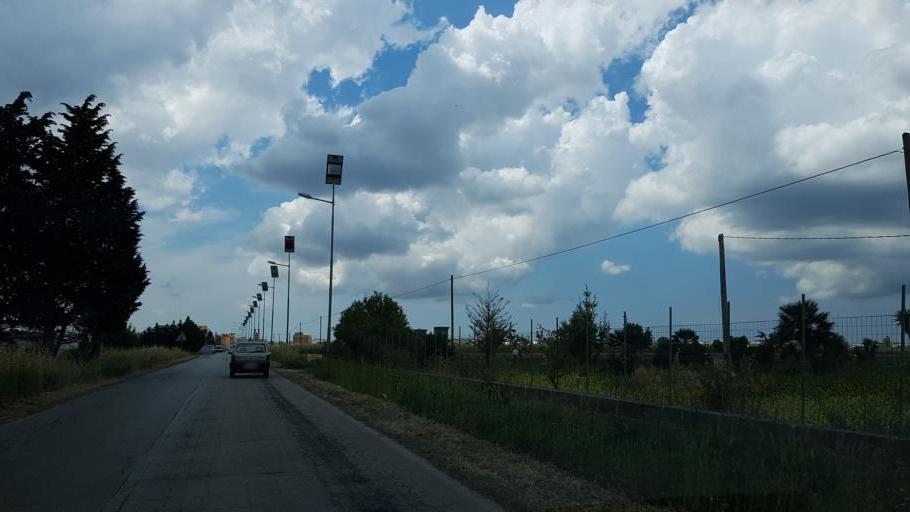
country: IT
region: Apulia
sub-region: Provincia di Brindisi
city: San Pancrazio Salentino
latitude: 40.4280
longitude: 17.8406
